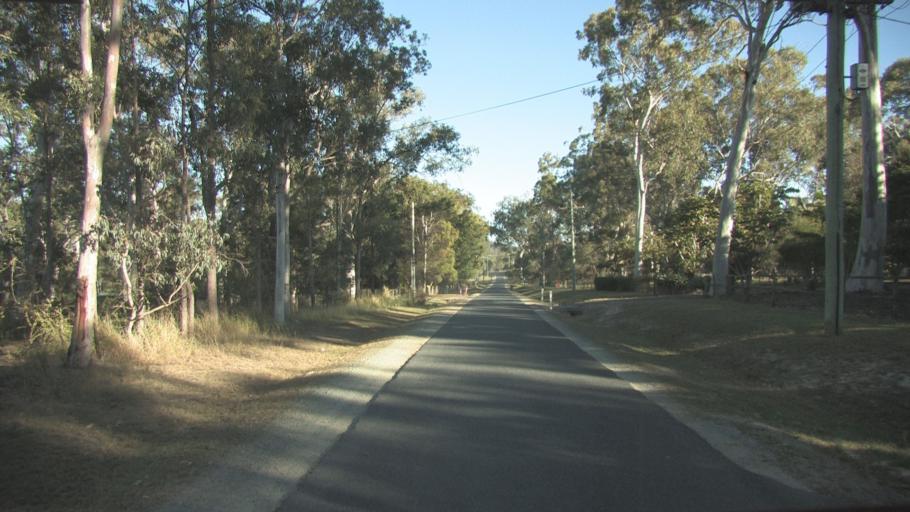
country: AU
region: Queensland
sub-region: Logan
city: Chambers Flat
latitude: -27.7875
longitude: 153.0860
